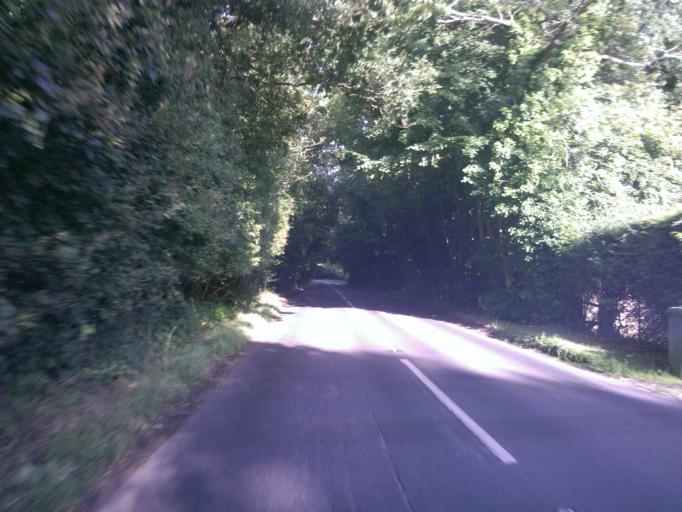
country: GB
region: England
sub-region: Kent
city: Sevenoaks
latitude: 51.1964
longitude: 0.1902
